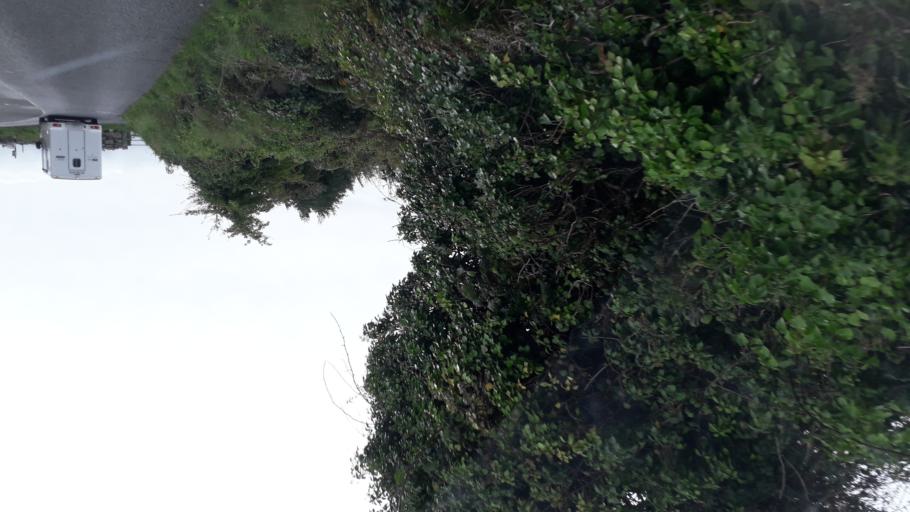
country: IE
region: Leinster
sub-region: Wicklow
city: Enniskerry
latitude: 53.2249
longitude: -6.2059
